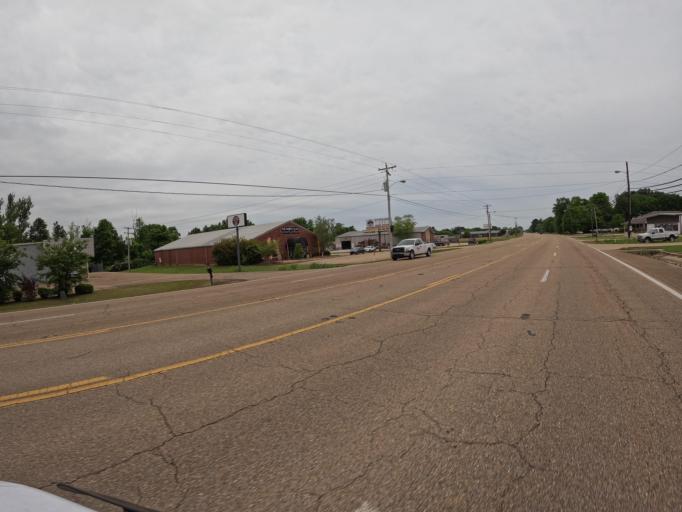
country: US
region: Mississippi
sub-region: Lee County
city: Tupelo
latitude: 34.2901
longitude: -88.7476
